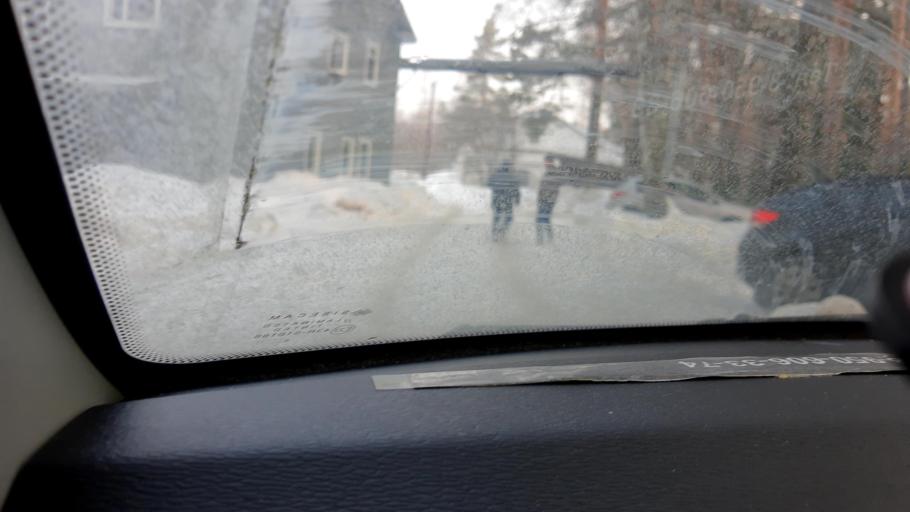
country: RU
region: Nizjnij Novgorod
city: Afonino
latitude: 56.1738
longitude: 44.0755
